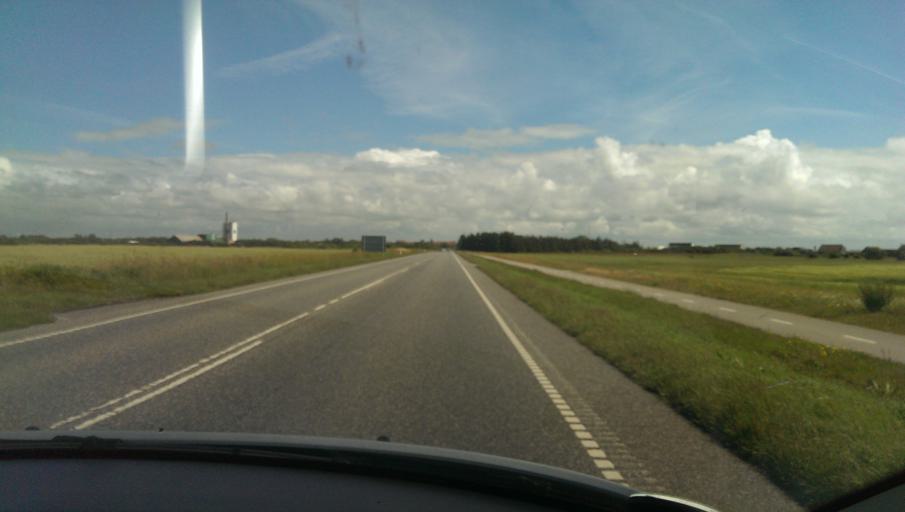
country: DK
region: Central Jutland
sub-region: Ringkobing-Skjern Kommune
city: Ringkobing
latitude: 56.1002
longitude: 8.2225
